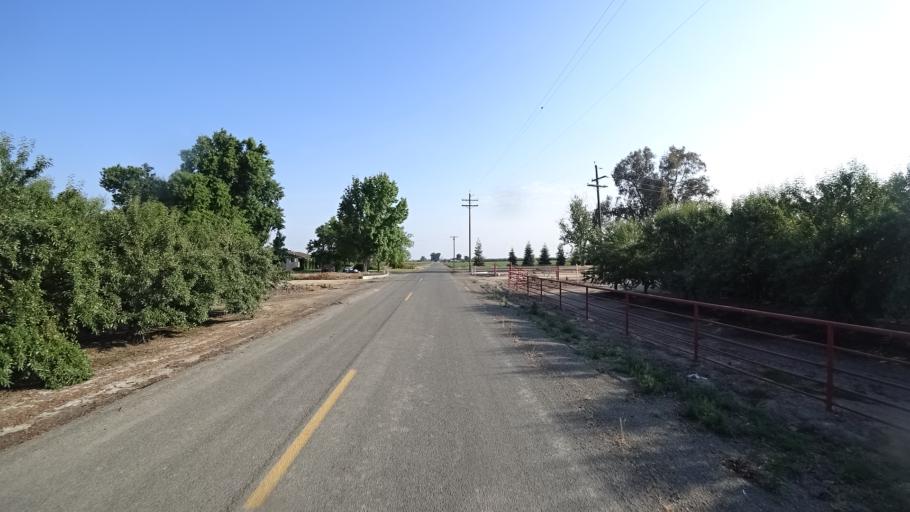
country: US
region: California
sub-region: Kings County
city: Lemoore
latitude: 36.3756
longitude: -119.7937
